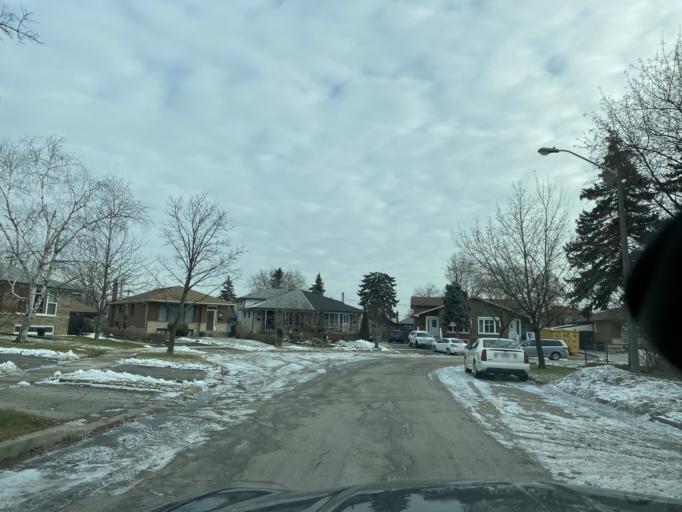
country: CA
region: Ontario
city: Etobicoke
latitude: 43.6597
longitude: -79.5752
